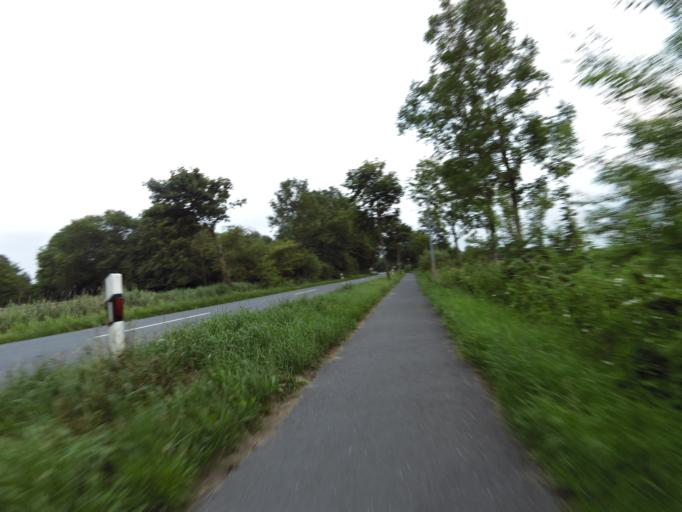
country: DE
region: Lower Saxony
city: Dorum
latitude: 53.7024
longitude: 8.5584
